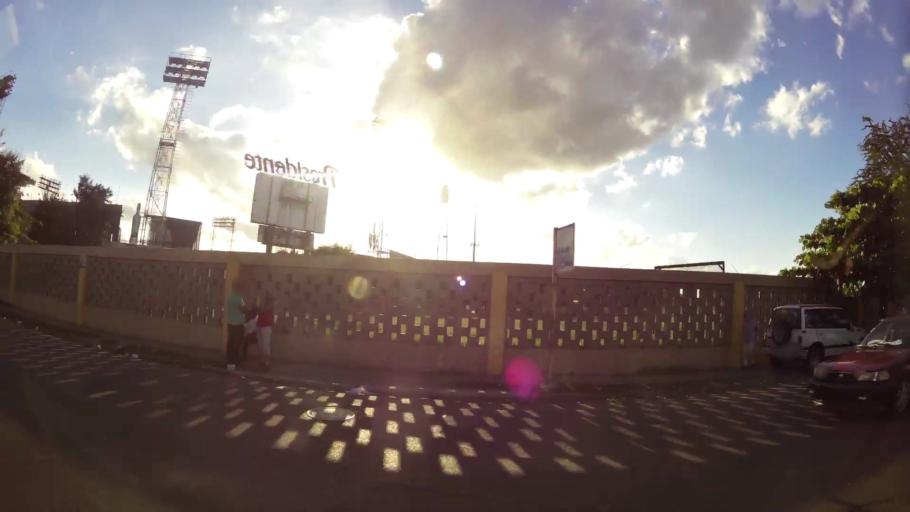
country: DO
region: Santiago
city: Santiago de los Caballeros
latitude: 19.4681
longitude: -70.7076
